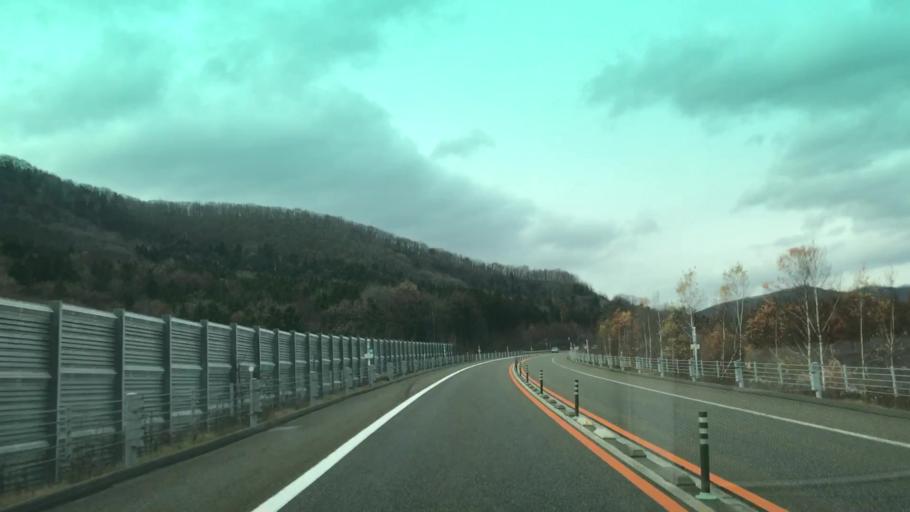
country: JP
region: Hokkaido
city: Otofuke
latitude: 43.0091
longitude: 142.8367
